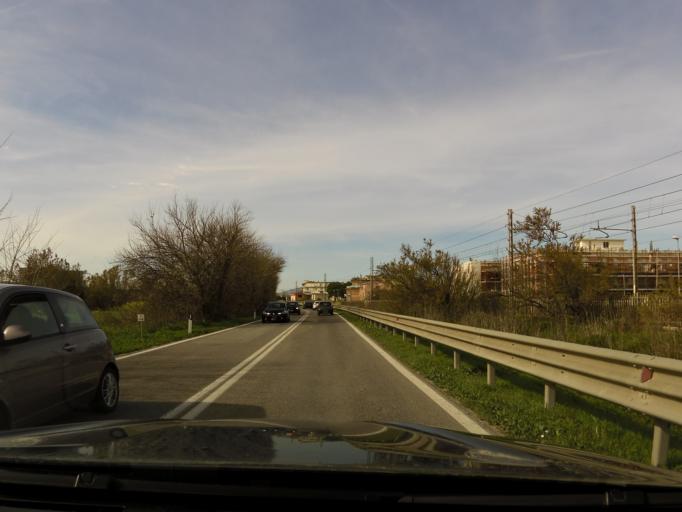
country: IT
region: The Marches
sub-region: Provincia di Macerata
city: Porto Recanati
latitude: 43.4102
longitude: 13.6757
